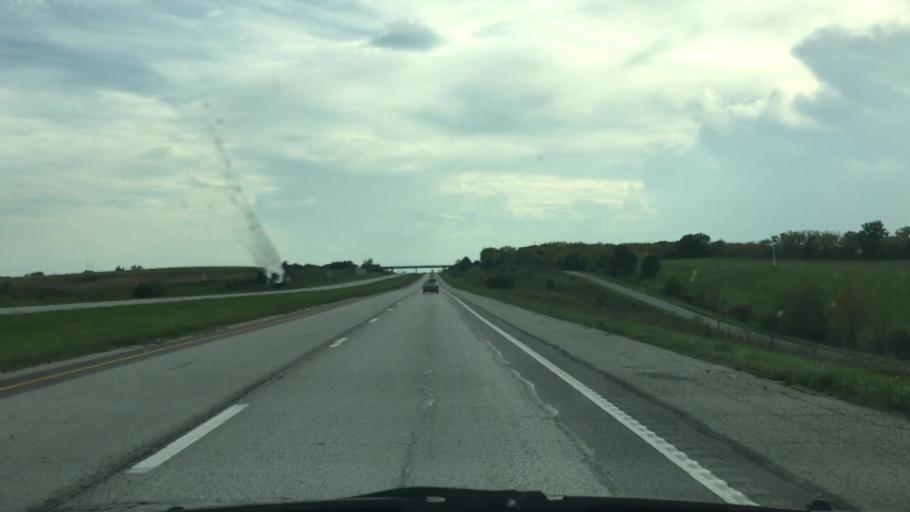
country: US
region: Missouri
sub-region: Harrison County
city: Bethany
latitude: 40.1444
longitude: -94.0411
